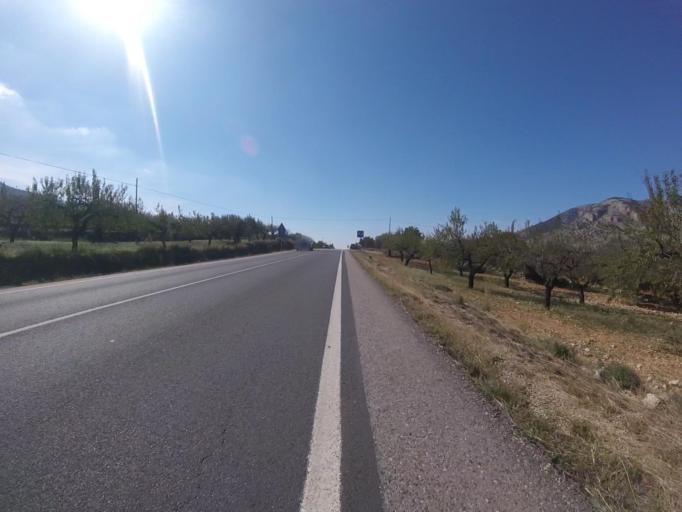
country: ES
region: Valencia
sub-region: Provincia de Castello
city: Sierra-Engarceran
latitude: 40.3045
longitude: -0.0421
